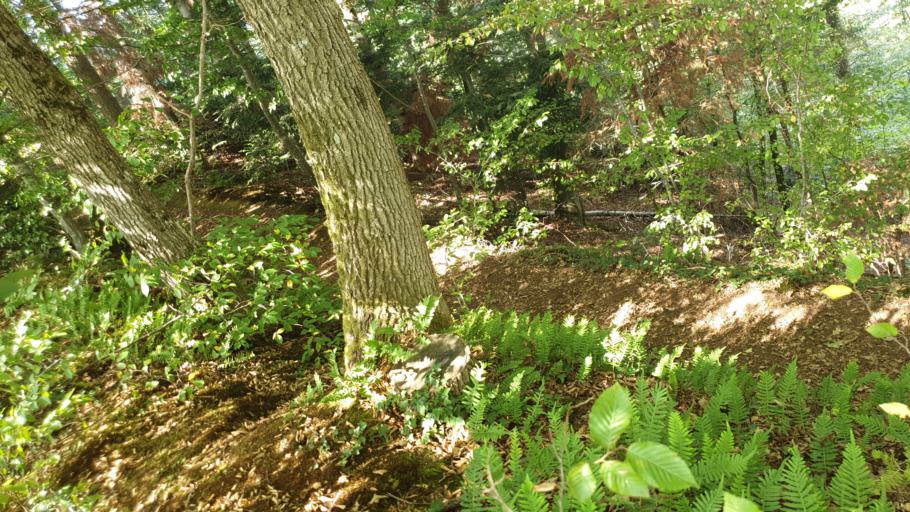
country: DE
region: Baden-Wuerttemberg
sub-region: Freiburg Region
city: Kirchzarten
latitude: 47.9572
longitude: 7.9469
